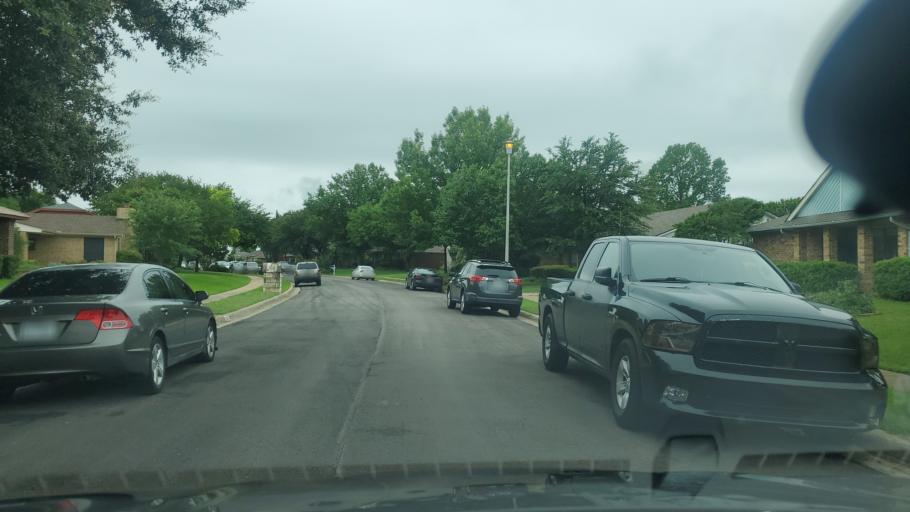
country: US
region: Texas
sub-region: Dallas County
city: Garland
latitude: 32.9397
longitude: -96.6278
